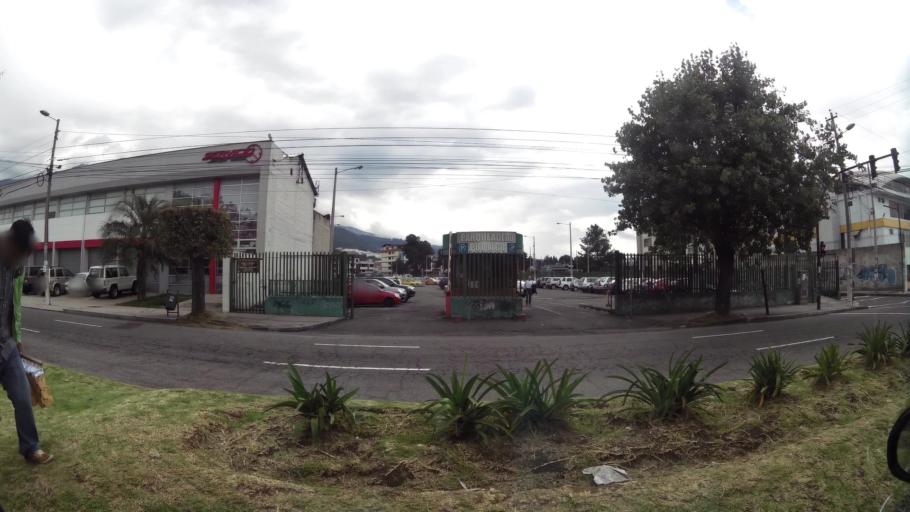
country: EC
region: Pichincha
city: Quito
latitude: -0.1654
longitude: -78.4849
